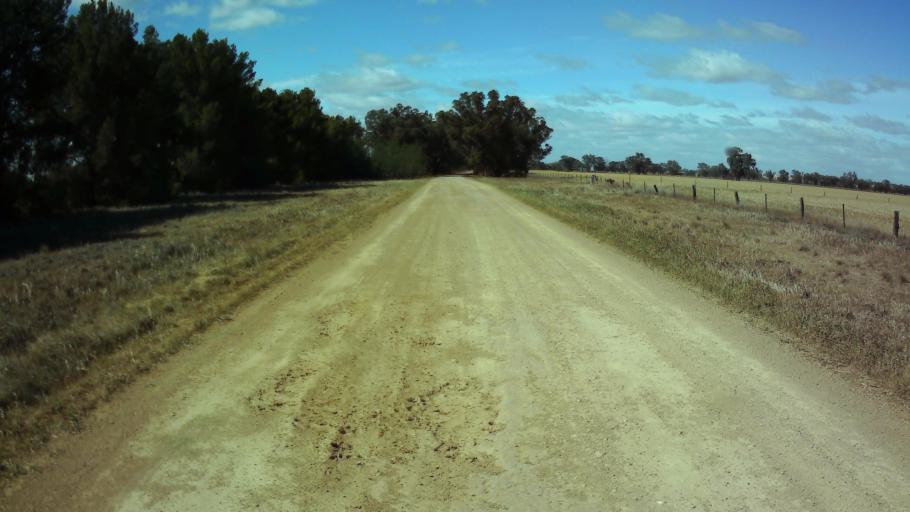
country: AU
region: New South Wales
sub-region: Weddin
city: Grenfell
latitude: -34.0348
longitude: 148.3168
